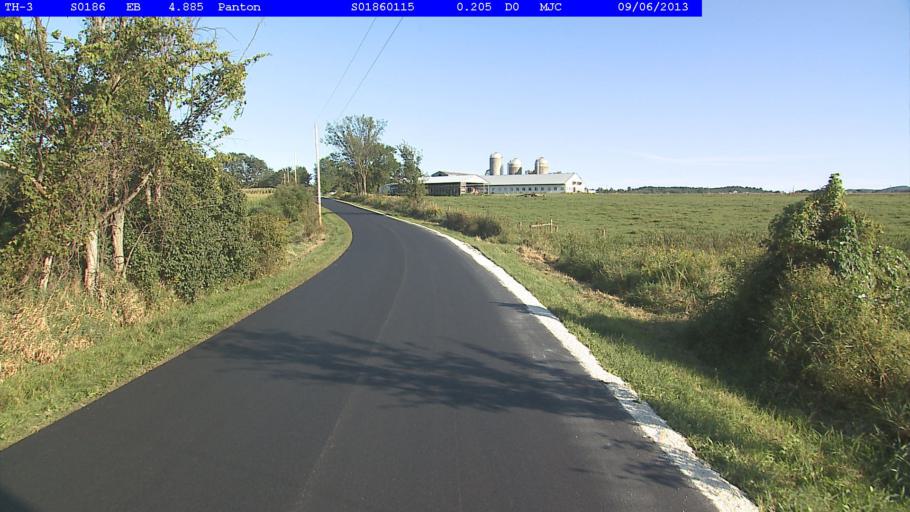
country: US
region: Vermont
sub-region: Addison County
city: Vergennes
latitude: 44.1611
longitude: -73.2899
